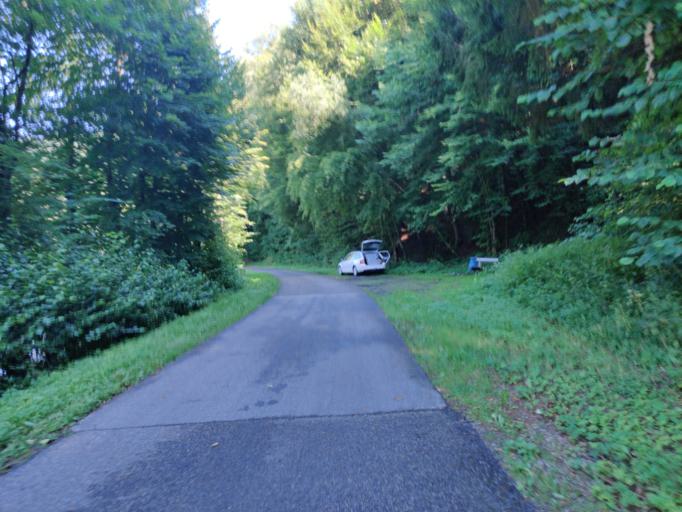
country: AT
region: Upper Austria
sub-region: Politischer Bezirk Rohrbach
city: Atzesberg
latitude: 48.4438
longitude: 13.8864
